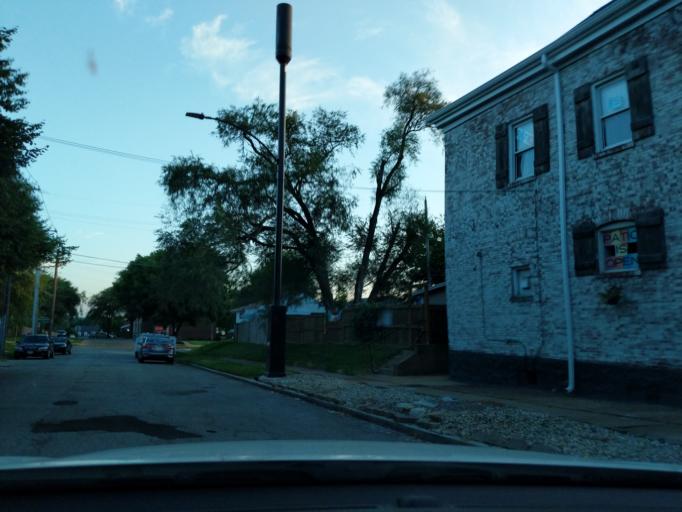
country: US
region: Missouri
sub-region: Saint Louis County
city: Maplewood
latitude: 38.6074
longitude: -90.2855
